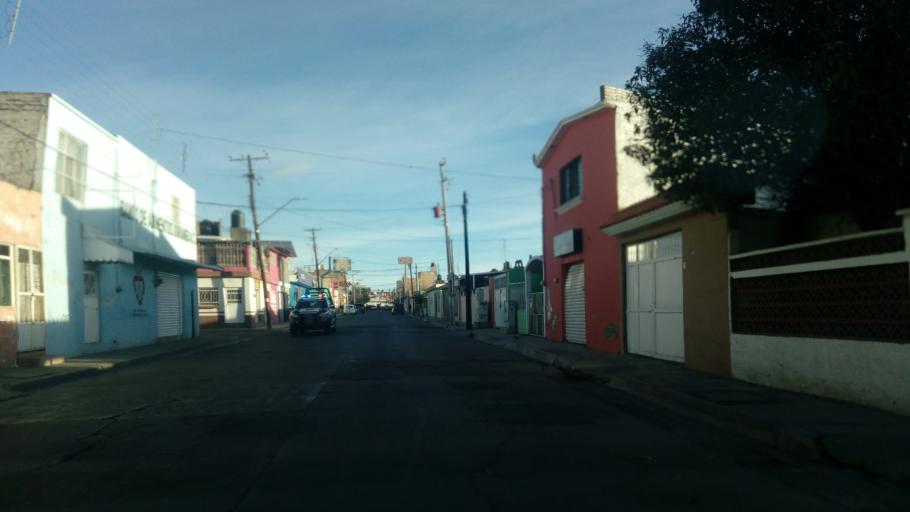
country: MX
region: Durango
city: Victoria de Durango
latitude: 24.0092
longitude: -104.6760
